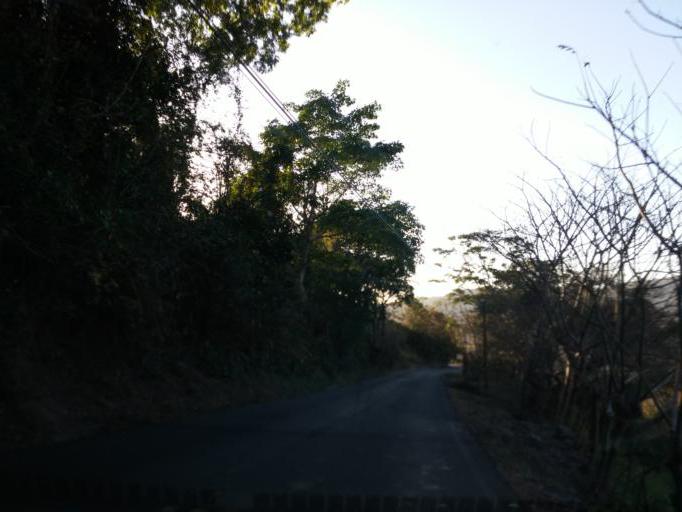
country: CR
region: Alajuela
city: Desamparados
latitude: 9.9552
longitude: -84.4807
